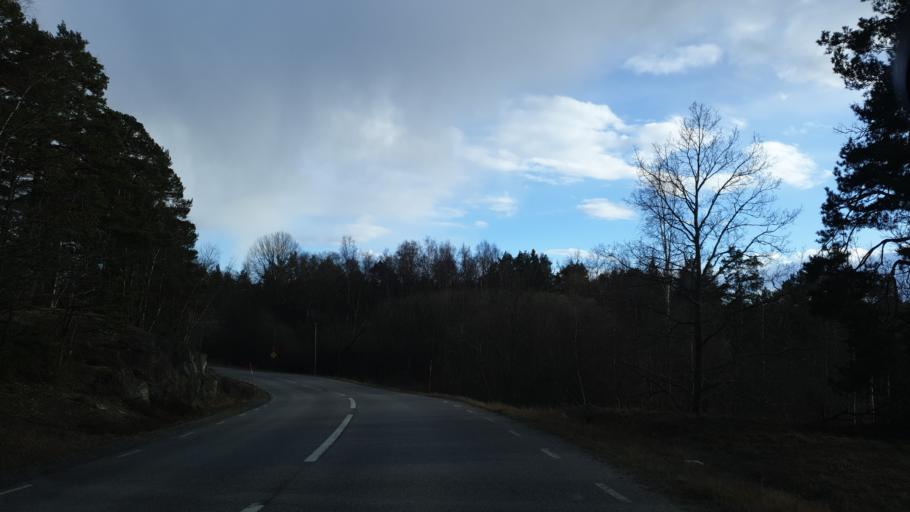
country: SE
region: Stockholm
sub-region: Varmdo Kommun
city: Holo
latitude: 59.3515
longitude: 18.7031
